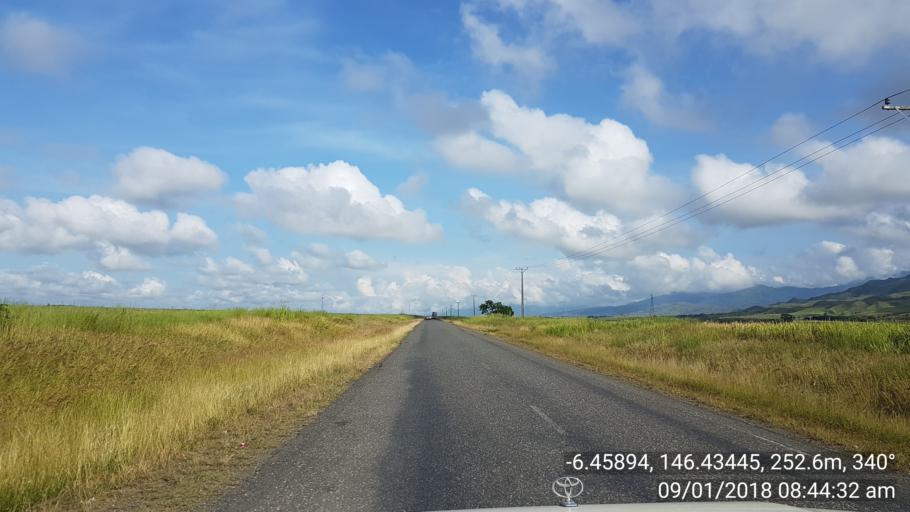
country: PG
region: Eastern Highlands
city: Kainantu
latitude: -6.4590
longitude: 146.4344
